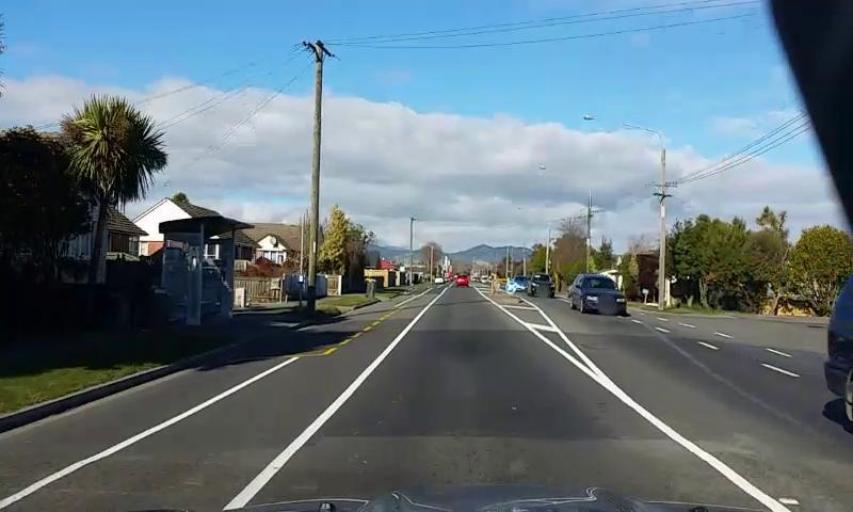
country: NZ
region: Canterbury
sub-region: Christchurch City
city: Christchurch
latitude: -43.5010
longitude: 172.6622
